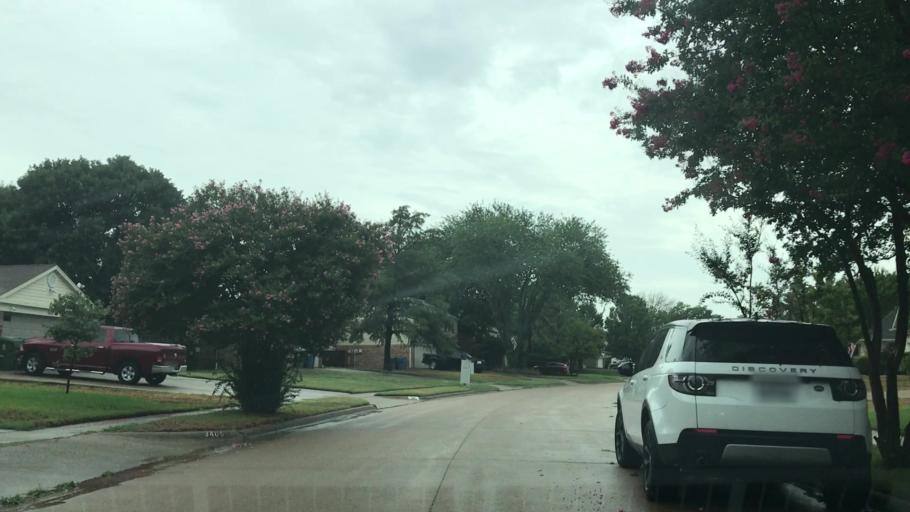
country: US
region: Texas
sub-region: Denton County
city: Flower Mound
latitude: 33.0406
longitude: -97.0574
